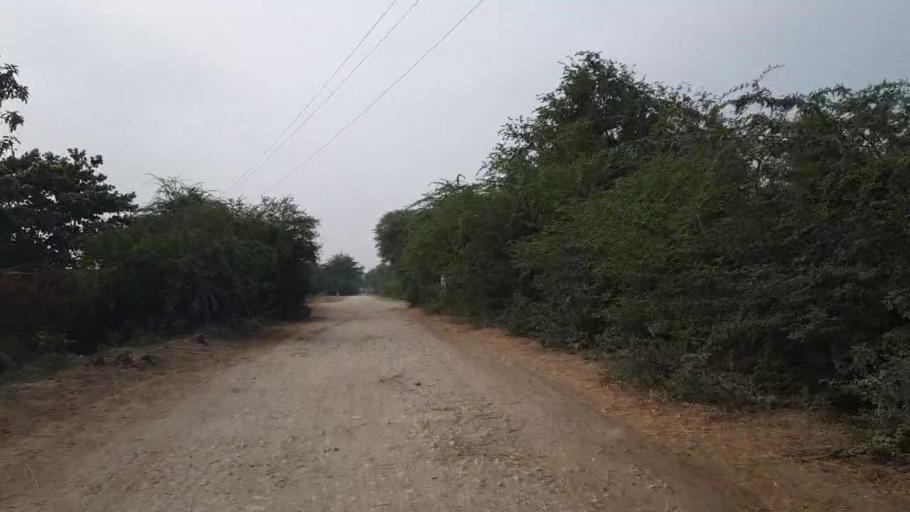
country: PK
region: Sindh
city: Matli
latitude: 24.9515
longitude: 68.5810
